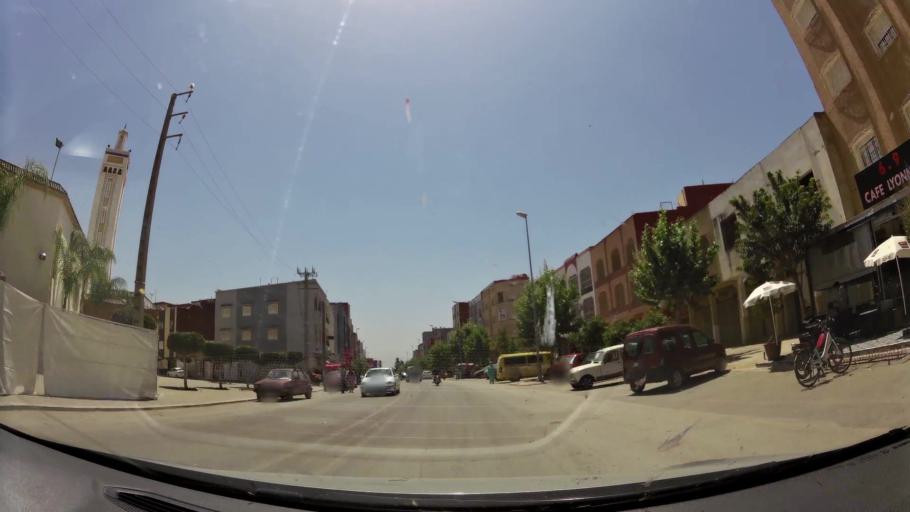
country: MA
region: Rabat-Sale-Zemmour-Zaer
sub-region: Khemisset
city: Khemisset
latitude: 33.8317
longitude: -6.0640
